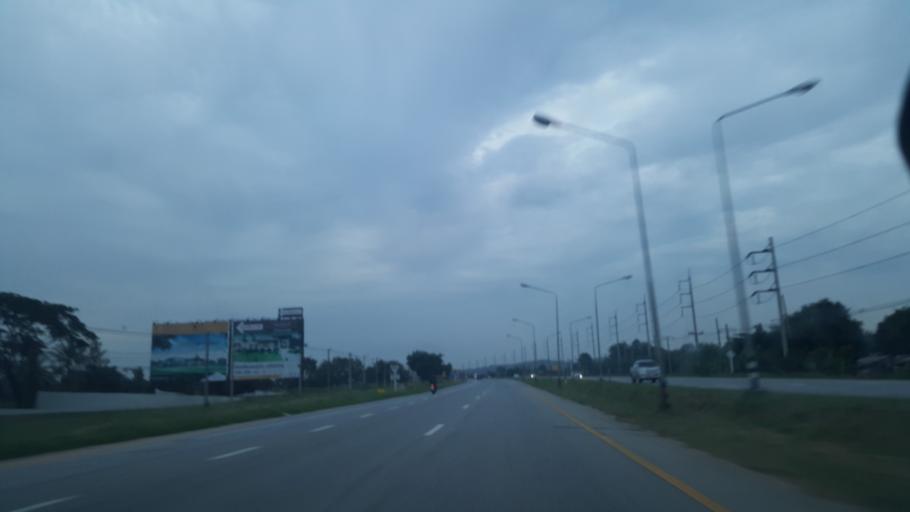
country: TH
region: Chon Buri
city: Phatthaya
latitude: 12.9236
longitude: 101.0331
